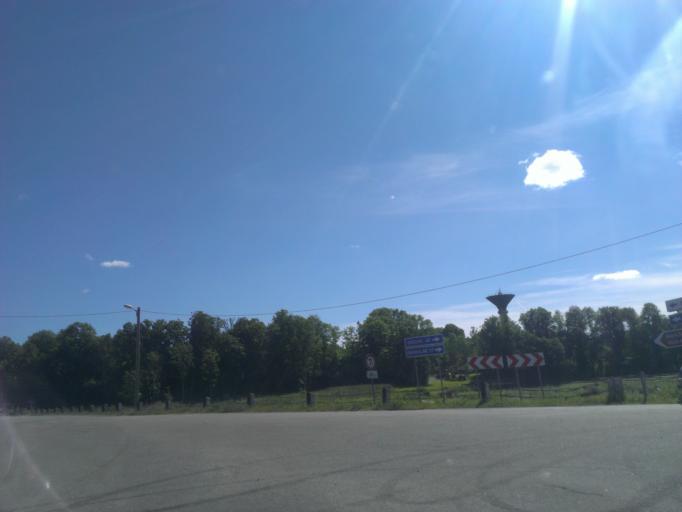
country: LV
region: Malpils
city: Malpils
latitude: 57.0112
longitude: 24.9462
